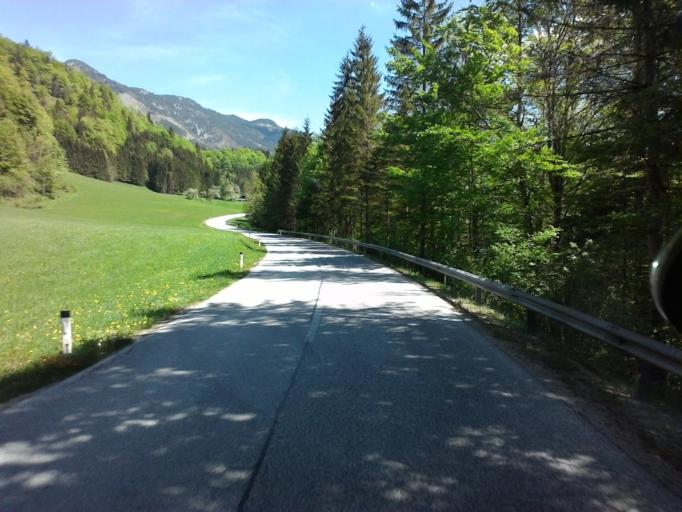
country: AT
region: Styria
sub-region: Politischer Bezirk Liezen
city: Palfau
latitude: 47.6931
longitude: 14.7799
